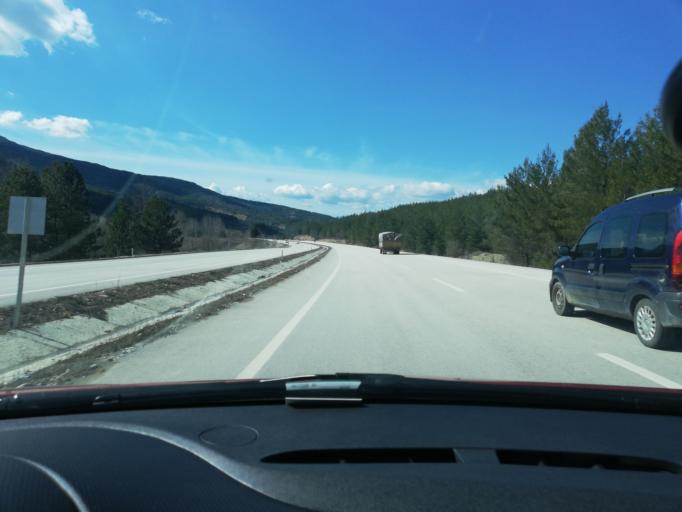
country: TR
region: Karabuk
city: Safranbolu
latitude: 41.2009
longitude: 32.8216
